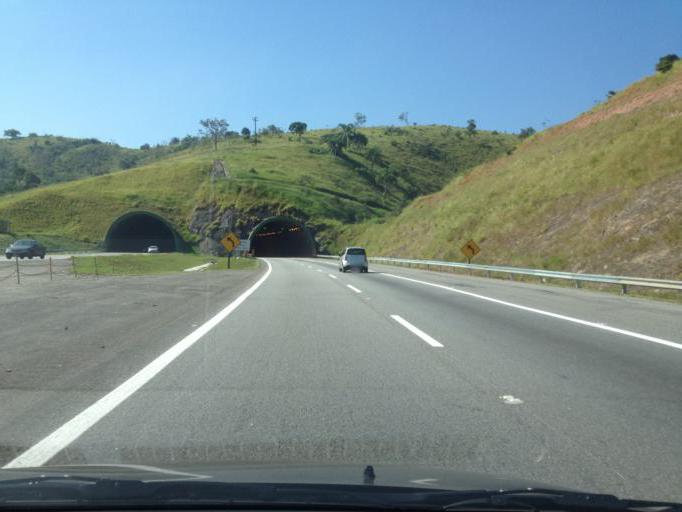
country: BR
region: Sao Paulo
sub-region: Jacarei
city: Jacarei
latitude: -23.3429
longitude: -45.9575
